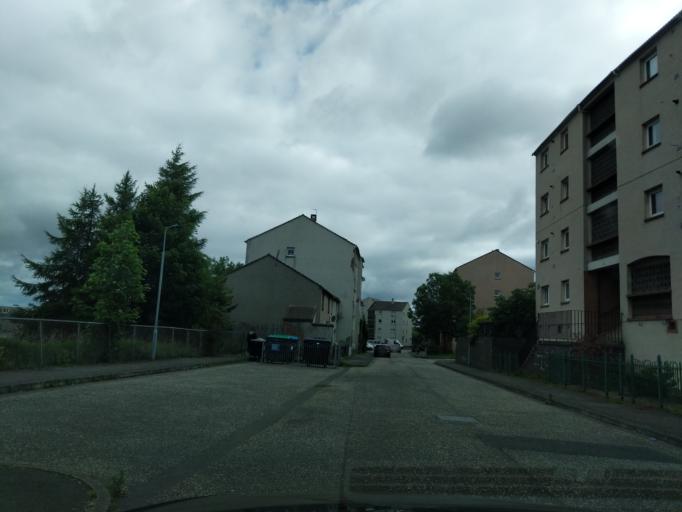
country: GB
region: Scotland
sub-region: Edinburgh
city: Colinton
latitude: 55.9181
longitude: -3.2834
